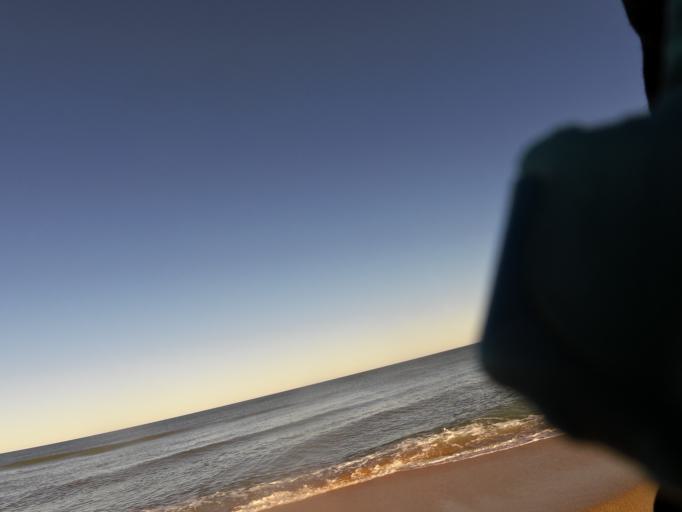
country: US
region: Florida
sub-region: Saint Johns County
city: Villano Beach
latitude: 29.9961
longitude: -81.3160
